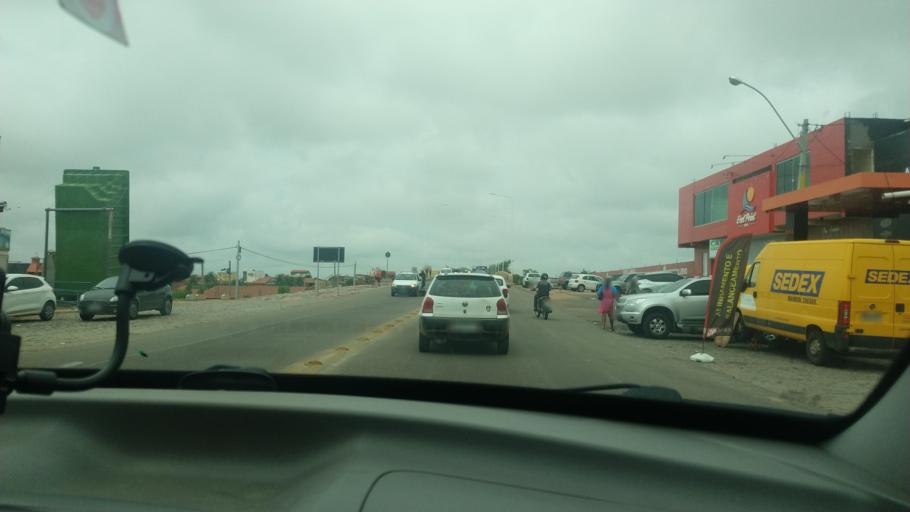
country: BR
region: Bahia
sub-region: Paulo Afonso
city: Paulo Afonso
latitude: -9.4003
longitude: -38.2332
